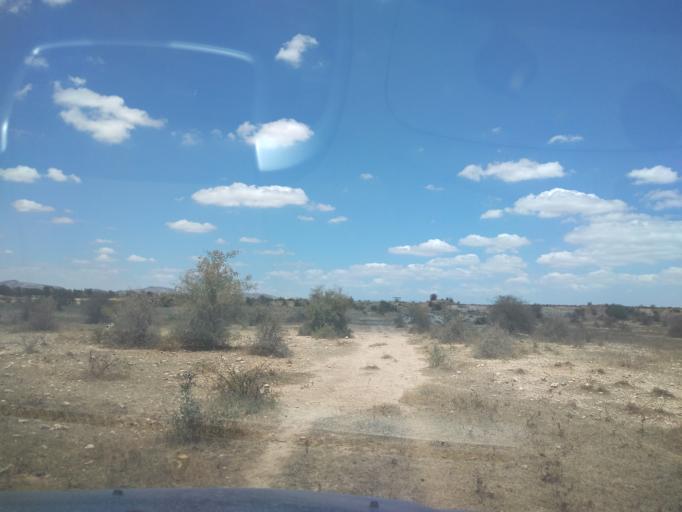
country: TN
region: Susah
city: Harqalah
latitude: 36.1723
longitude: 10.4403
